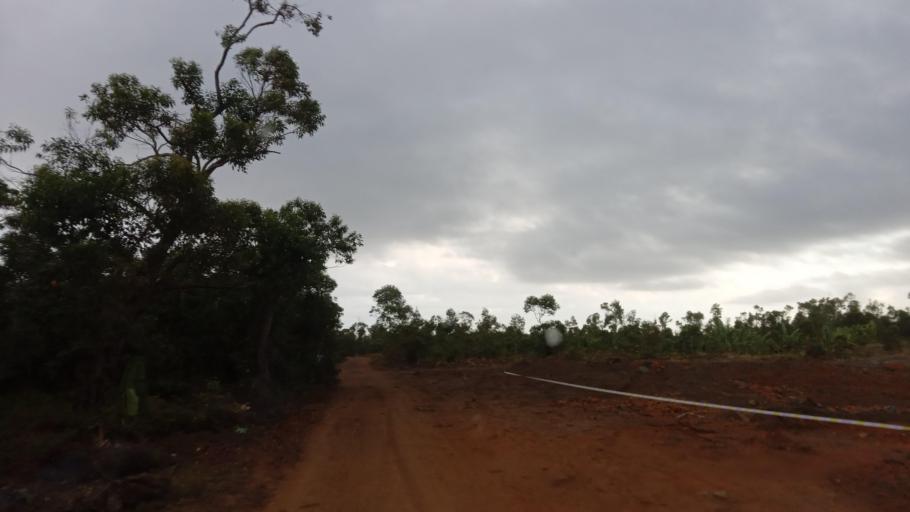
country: MG
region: Atsimo-Atsinanana
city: Vohipaho
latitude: -23.6182
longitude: 47.6037
